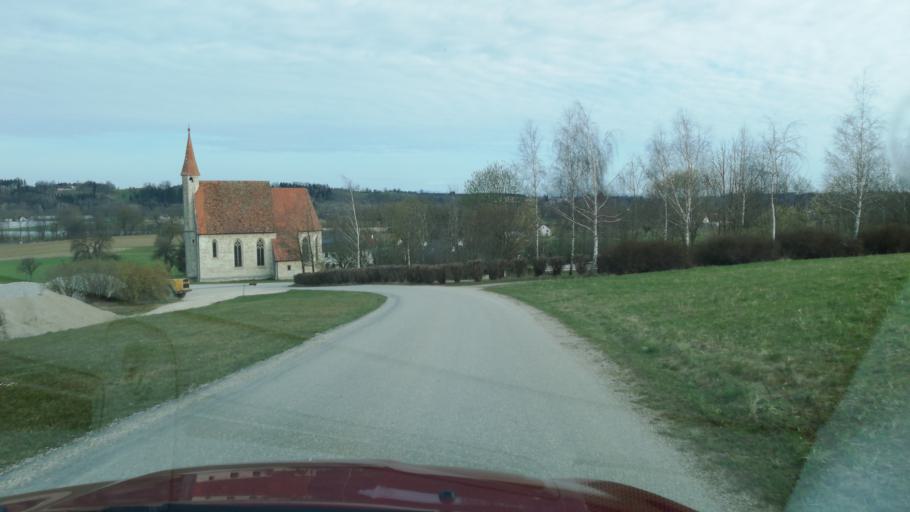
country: AT
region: Upper Austria
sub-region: Politischer Bezirk Steyr-Land
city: Pfarrkirchen bei Bad Hall
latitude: 48.0569
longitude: 14.1707
